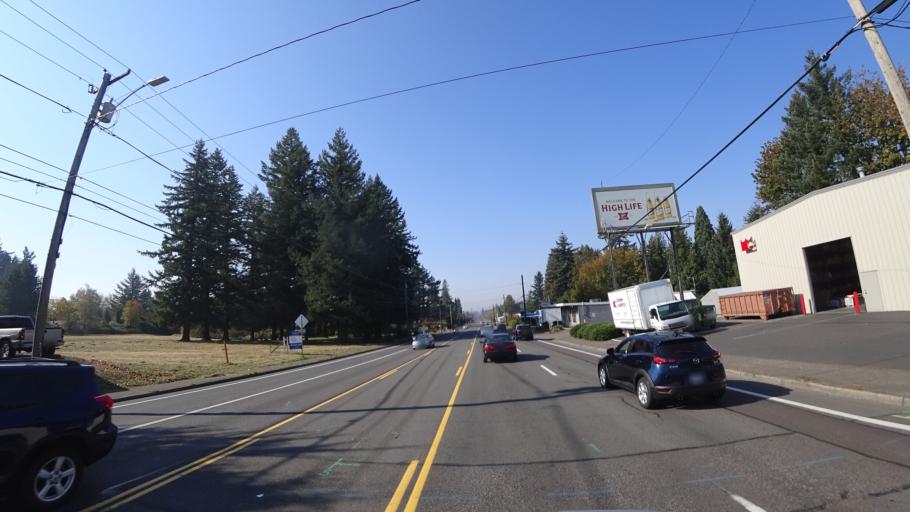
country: US
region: Oregon
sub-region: Multnomah County
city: Fairview
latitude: 45.5191
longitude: -122.4396
